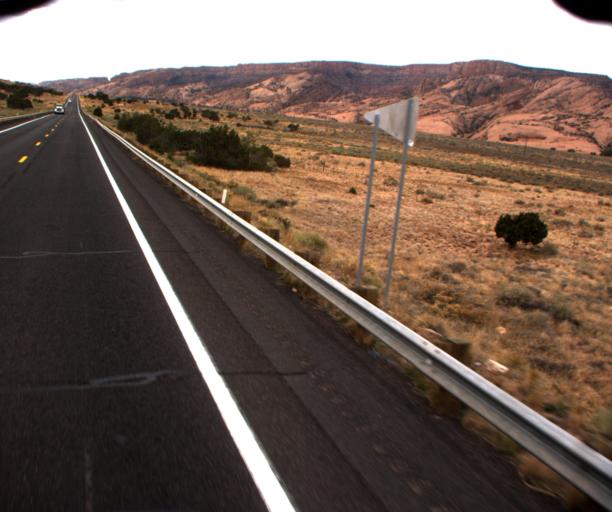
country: US
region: Arizona
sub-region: Navajo County
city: Kayenta
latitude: 36.6824
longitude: -110.3834
